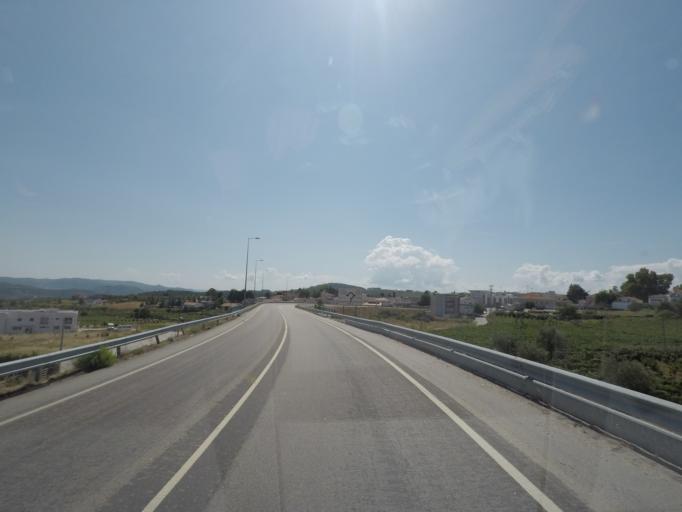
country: PT
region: Vila Real
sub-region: Sabrosa
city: Sabrosa
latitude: 41.2793
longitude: -7.4723
